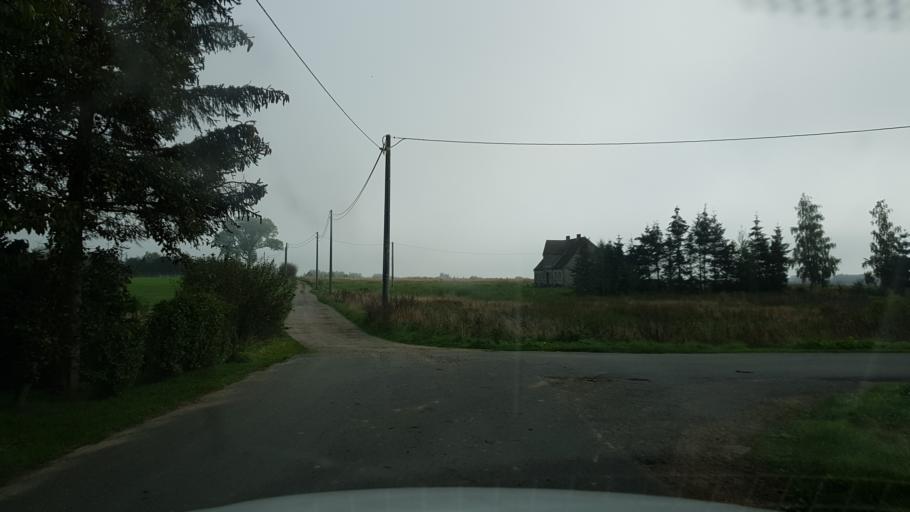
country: PL
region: West Pomeranian Voivodeship
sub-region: Powiat koszalinski
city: Mielno
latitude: 54.2299
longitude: 15.9451
